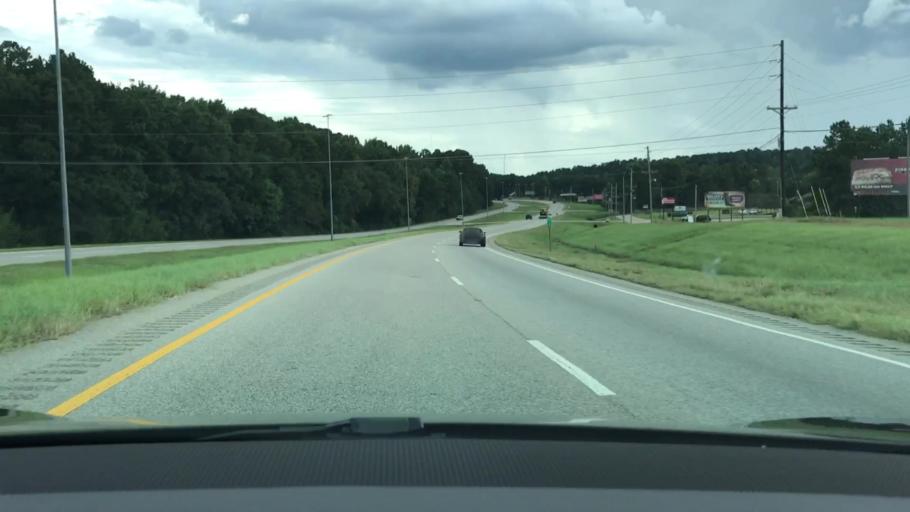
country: US
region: Alabama
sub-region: Pike County
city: Troy
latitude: 31.8317
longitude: -85.9914
